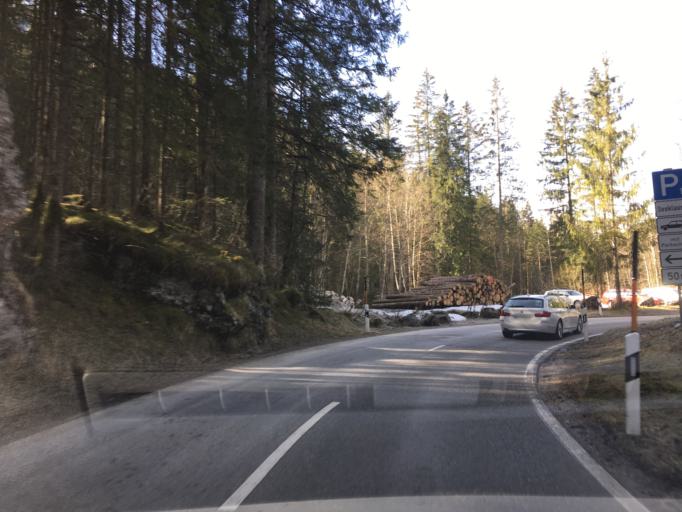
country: DE
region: Bavaria
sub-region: Upper Bavaria
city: Ramsau
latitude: 47.6048
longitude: 12.8593
